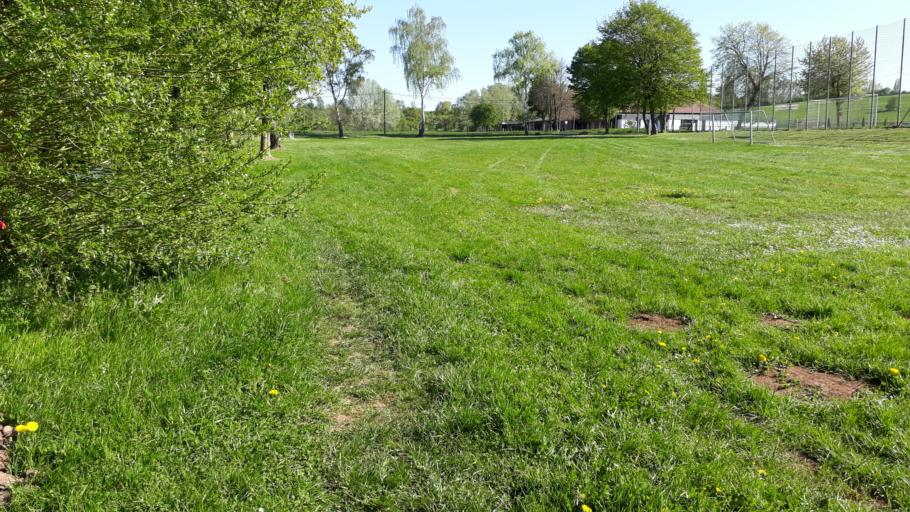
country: DE
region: North Rhine-Westphalia
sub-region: Regierungsbezirk Koln
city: Mechernich
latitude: 50.6408
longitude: 6.6490
